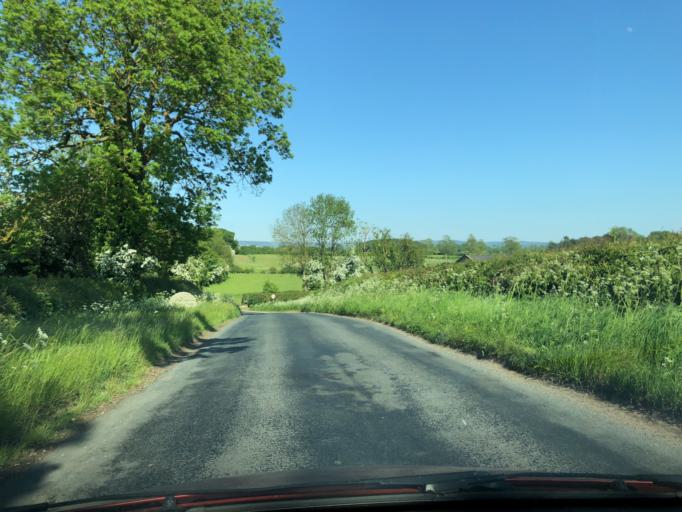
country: GB
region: England
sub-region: North Yorkshire
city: Northallerton
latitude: 54.3064
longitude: -1.3936
